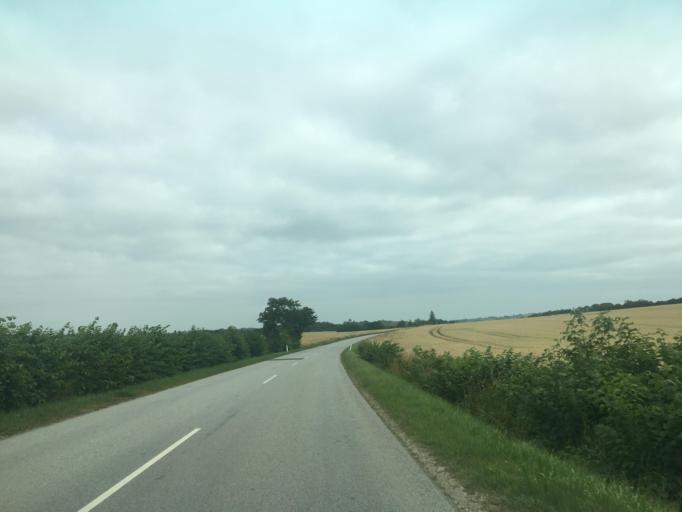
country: DK
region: North Denmark
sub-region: Thisted Kommune
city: Thisted
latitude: 56.8580
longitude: 8.6071
